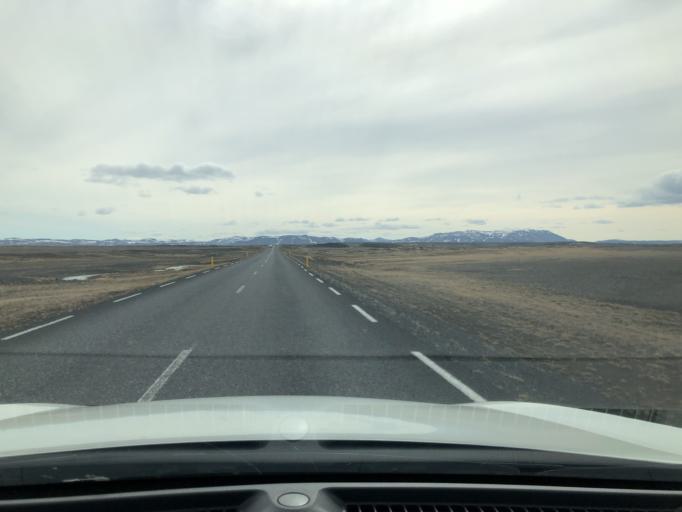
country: IS
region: Northeast
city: Laugar
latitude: 65.6304
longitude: -16.2644
